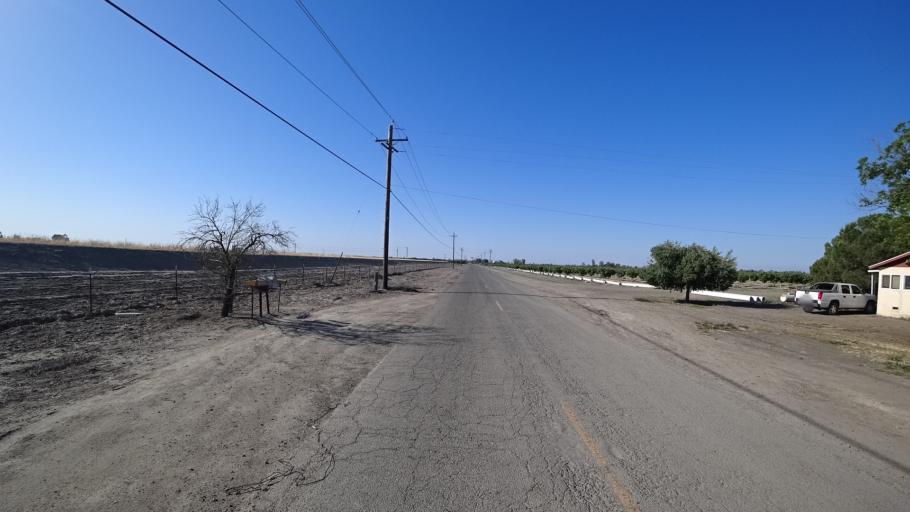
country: US
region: California
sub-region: Kings County
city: Corcoran
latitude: 36.1267
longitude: -119.5543
